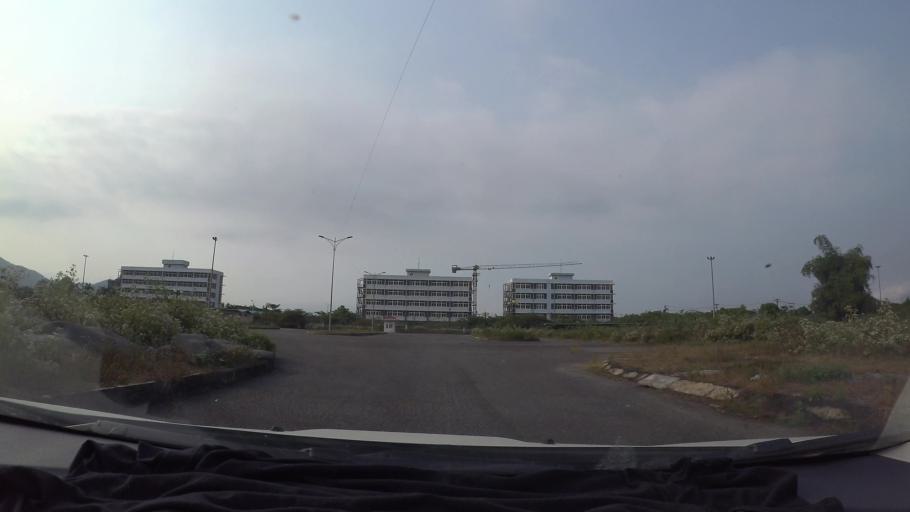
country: VN
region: Da Nang
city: Lien Chieu
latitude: 16.0478
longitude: 108.1601
